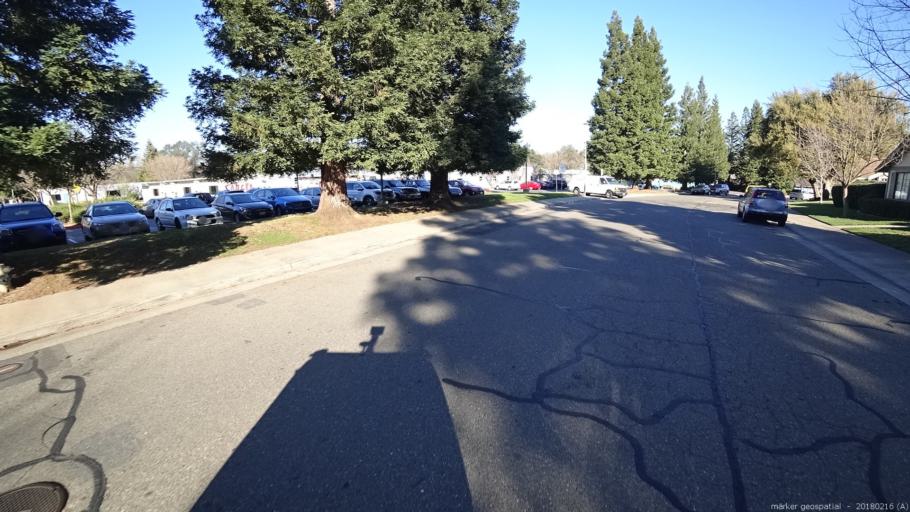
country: US
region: California
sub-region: Sacramento County
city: Gold River
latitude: 38.6264
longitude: -121.2479
